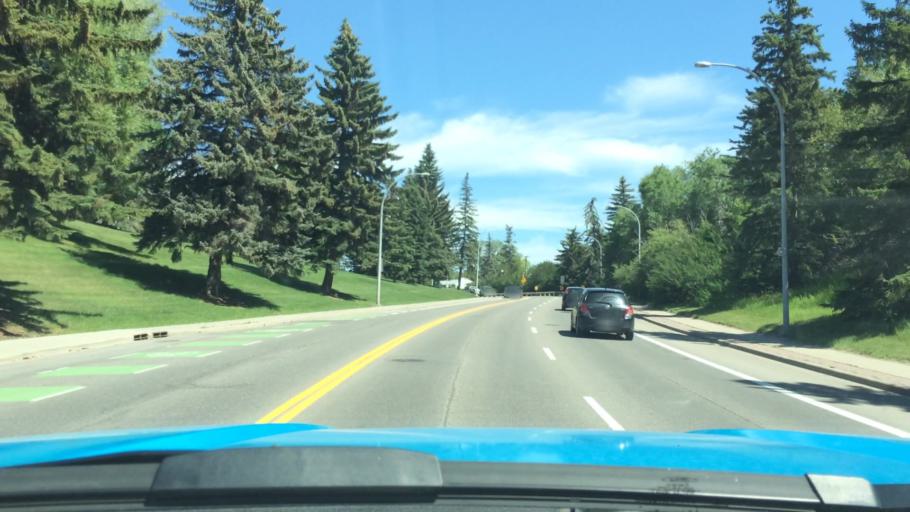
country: CA
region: Alberta
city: Calgary
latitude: 51.0622
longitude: -114.0854
